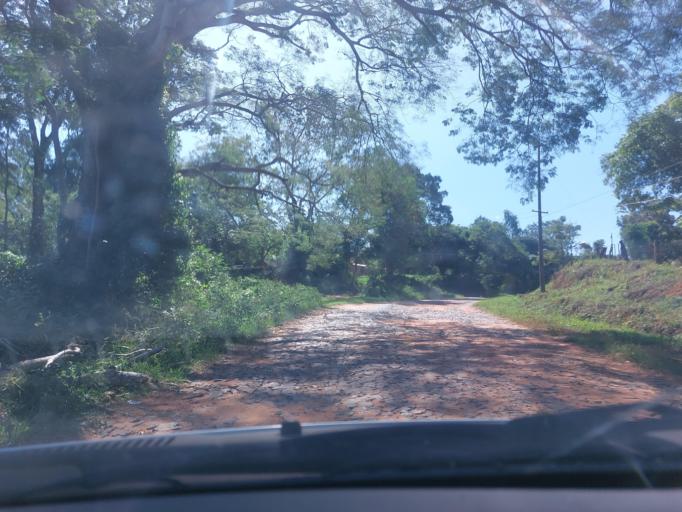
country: PY
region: San Pedro
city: Itacurubi del Rosario
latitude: -24.5810
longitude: -56.6008
